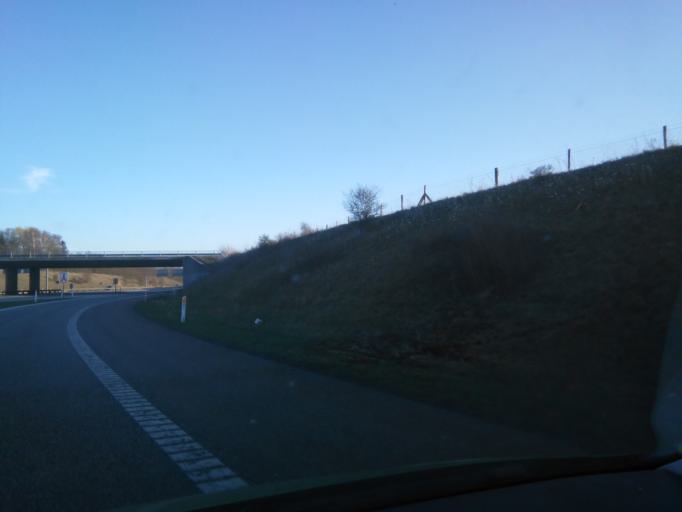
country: DK
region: Central Jutland
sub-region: Arhus Kommune
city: Framlev
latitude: 56.1542
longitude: 10.0439
